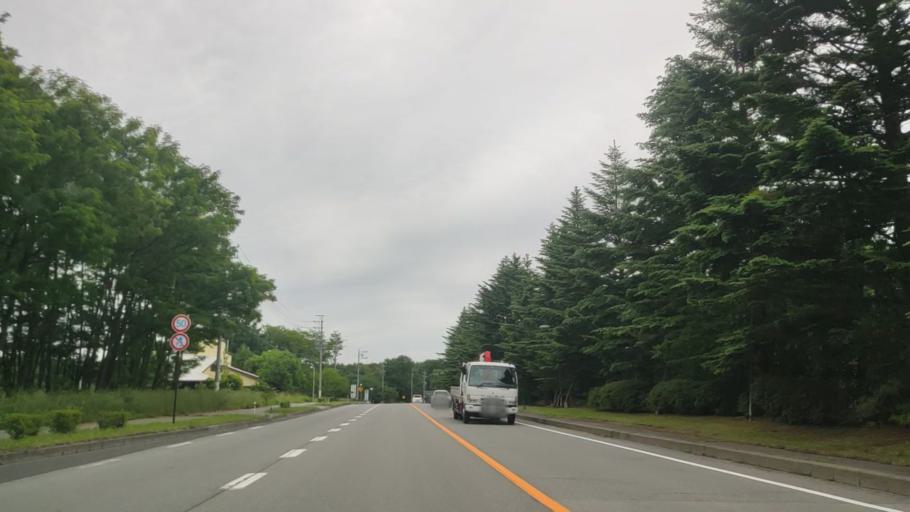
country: JP
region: Nagano
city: Komoro
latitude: 36.3351
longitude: 138.5296
